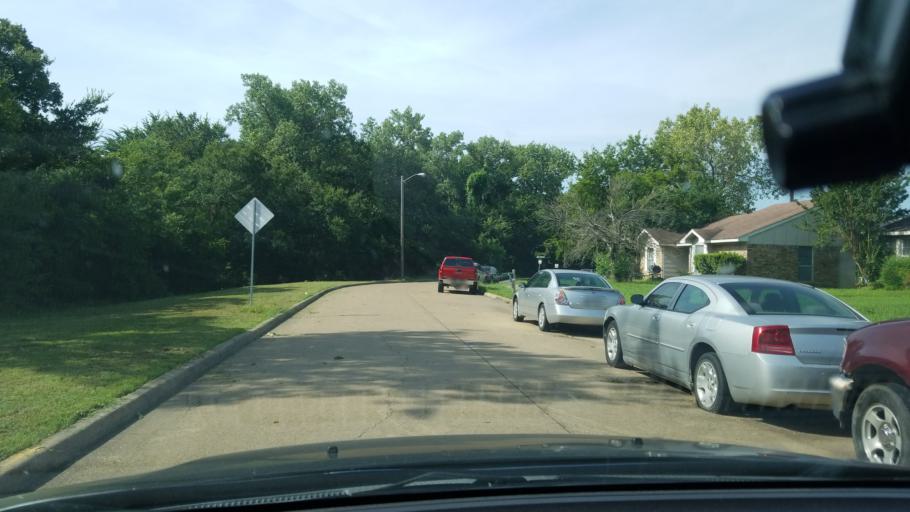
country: US
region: Texas
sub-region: Dallas County
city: Balch Springs
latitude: 32.7252
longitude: -96.6463
